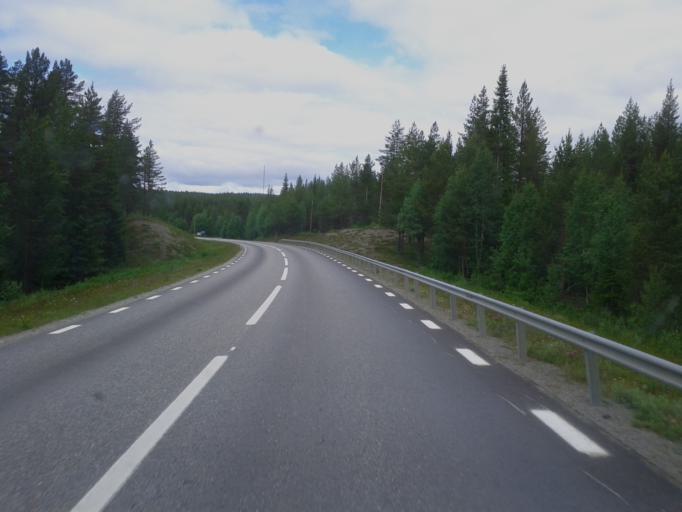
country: SE
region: Vaesterbotten
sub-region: Storumans Kommun
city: Fristad
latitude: 65.3811
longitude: 16.5118
